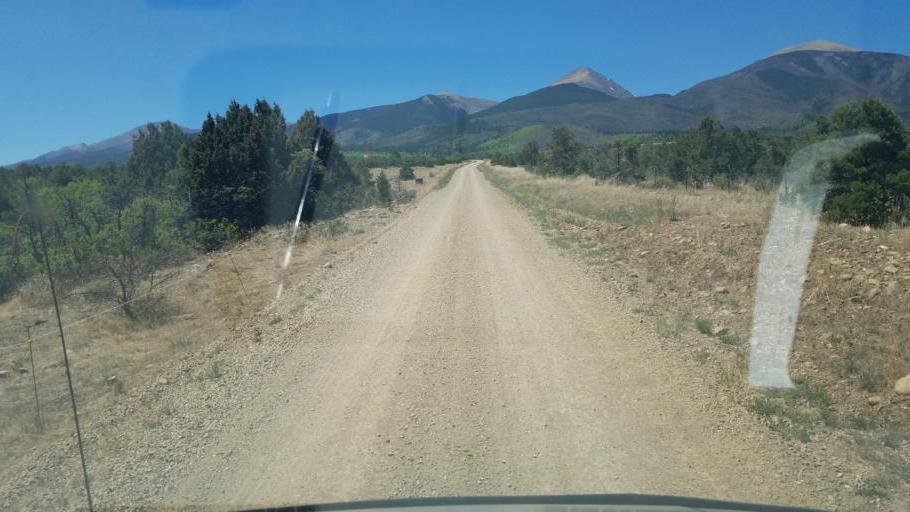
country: US
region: Colorado
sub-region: Custer County
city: Westcliffe
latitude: 38.3009
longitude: -105.6688
